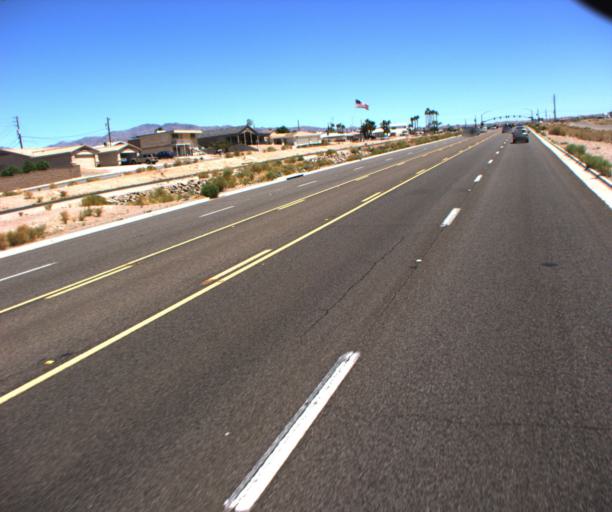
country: US
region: Arizona
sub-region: Mohave County
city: Lake Havasu City
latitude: 34.4537
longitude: -114.3020
